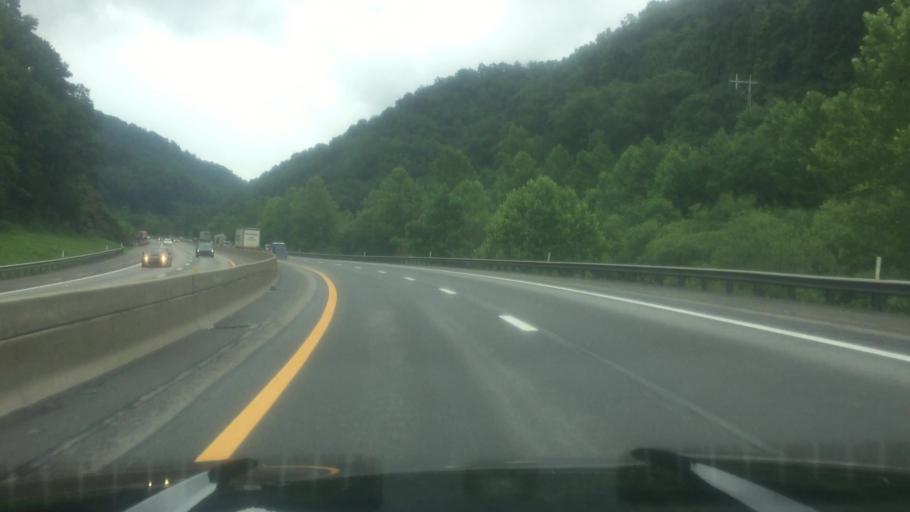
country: US
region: West Virginia
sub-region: Kanawha County
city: Montgomery
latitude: 38.0088
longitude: -81.3492
